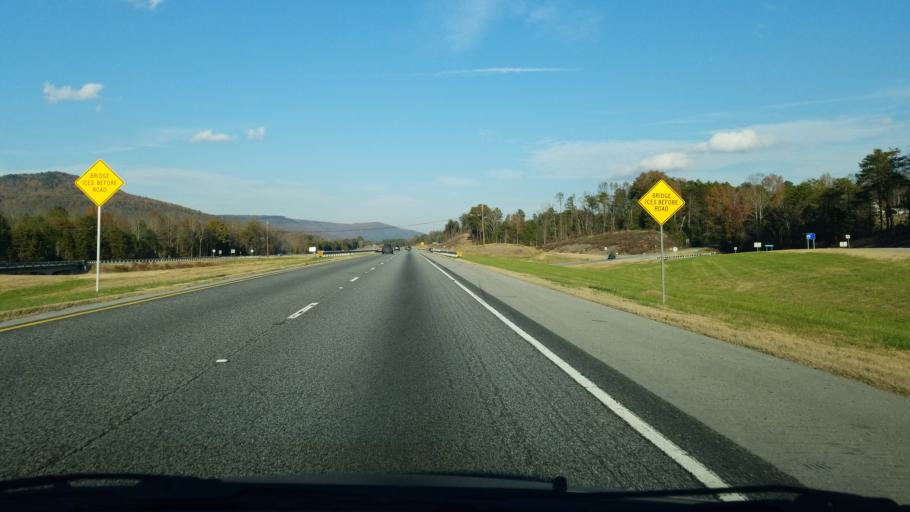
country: US
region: Georgia
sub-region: Dade County
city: Trenton
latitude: 34.9413
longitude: -85.4768
